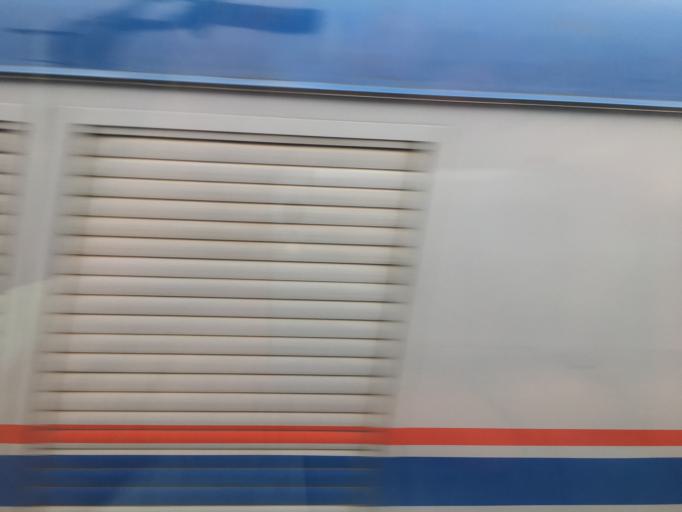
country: TM
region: Mary
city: Yoloeten
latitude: 36.4597
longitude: 62.5934
